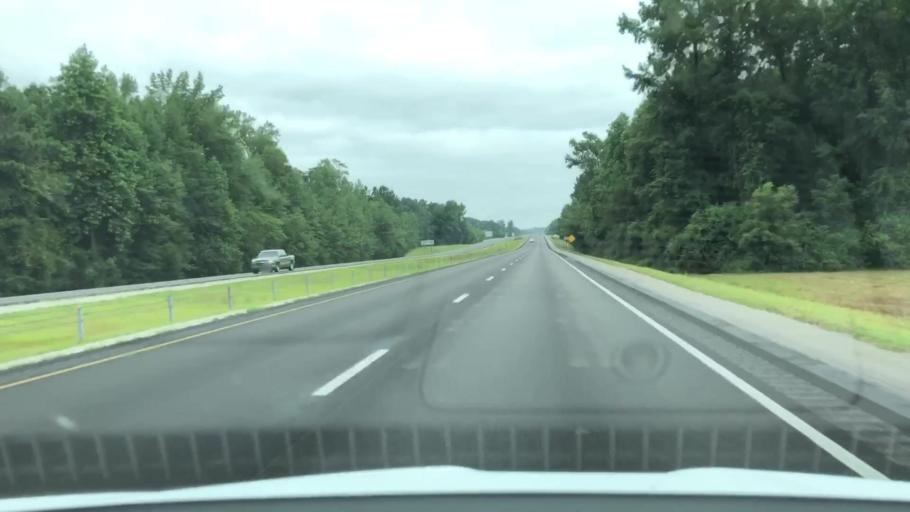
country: US
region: North Carolina
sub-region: Wayne County
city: Fremont
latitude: 35.5572
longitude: -77.9871
